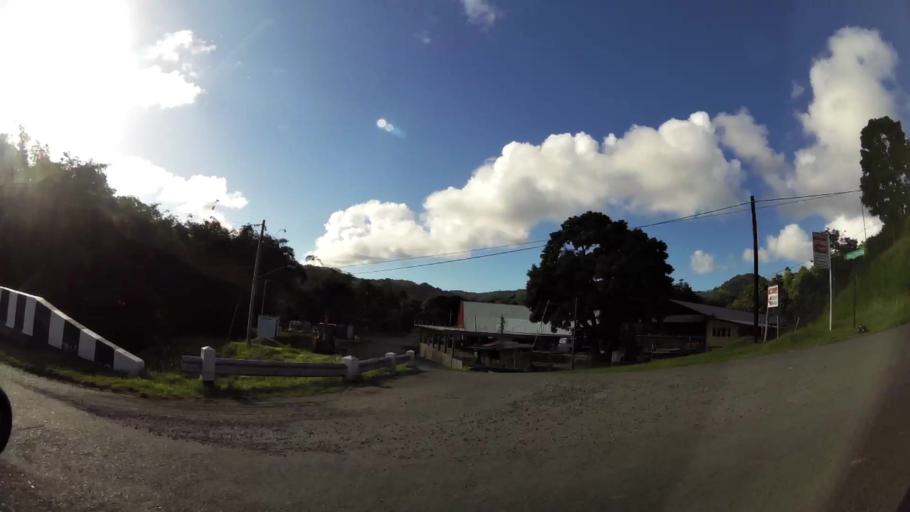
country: TT
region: Eastern Tobago
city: Roxborough
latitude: 11.2270
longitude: -60.6105
